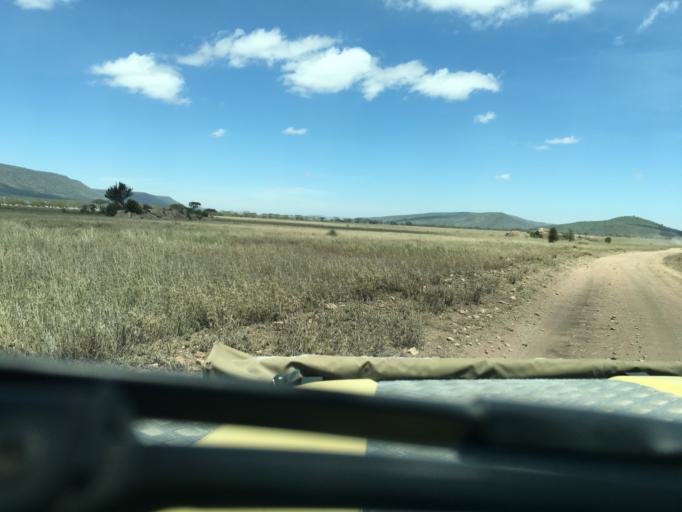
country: TZ
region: Simiyu
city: Kisesa
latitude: -2.6910
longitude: 34.7814
